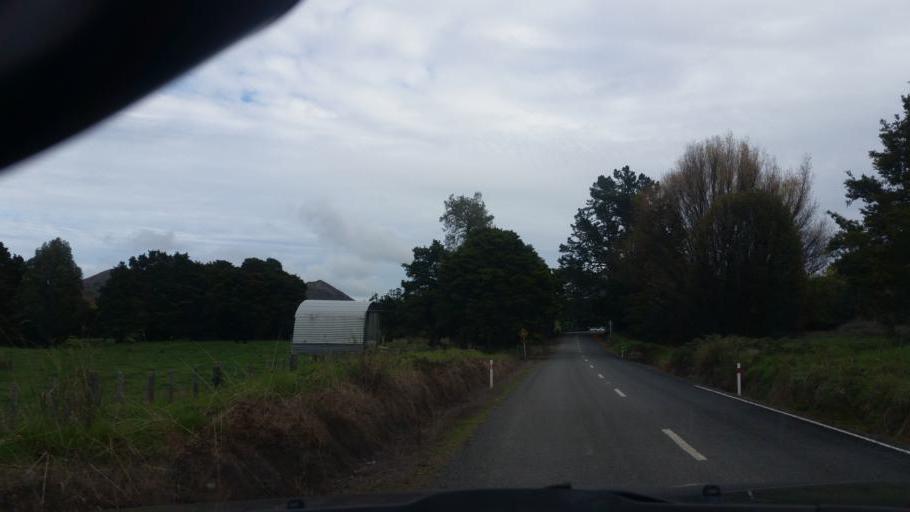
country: NZ
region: Northland
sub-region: Kaipara District
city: Dargaville
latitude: -35.7513
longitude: 173.9034
